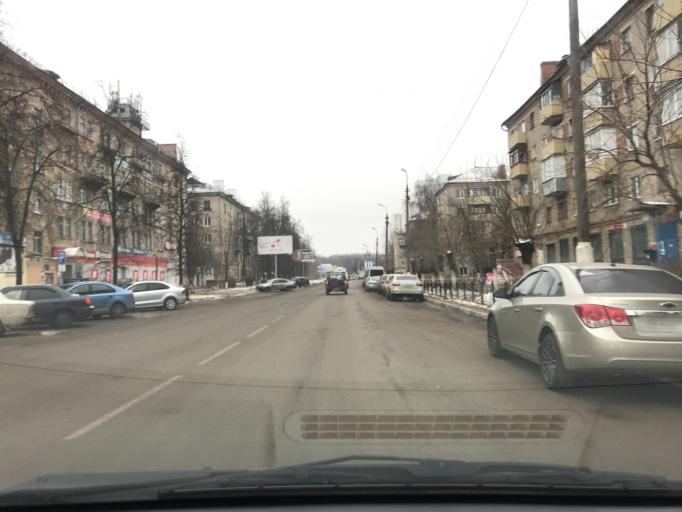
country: RU
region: Moskovskaya
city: Elektrostal'
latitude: 55.7979
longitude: 38.4385
